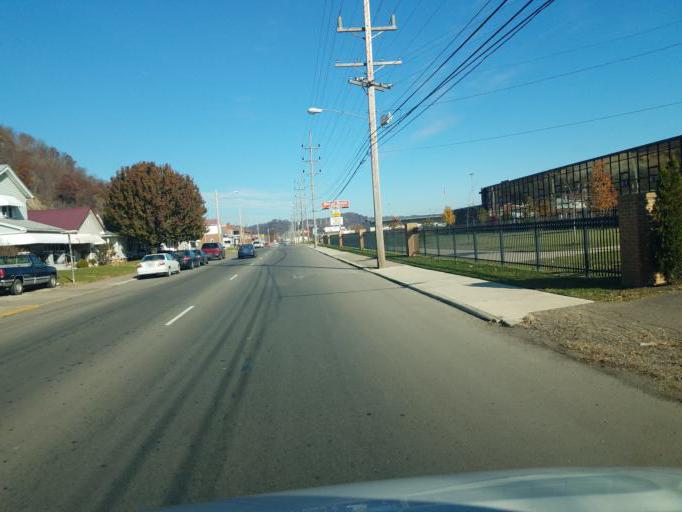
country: US
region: Ohio
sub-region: Scioto County
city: New Boston
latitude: 38.7450
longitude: -82.9487
